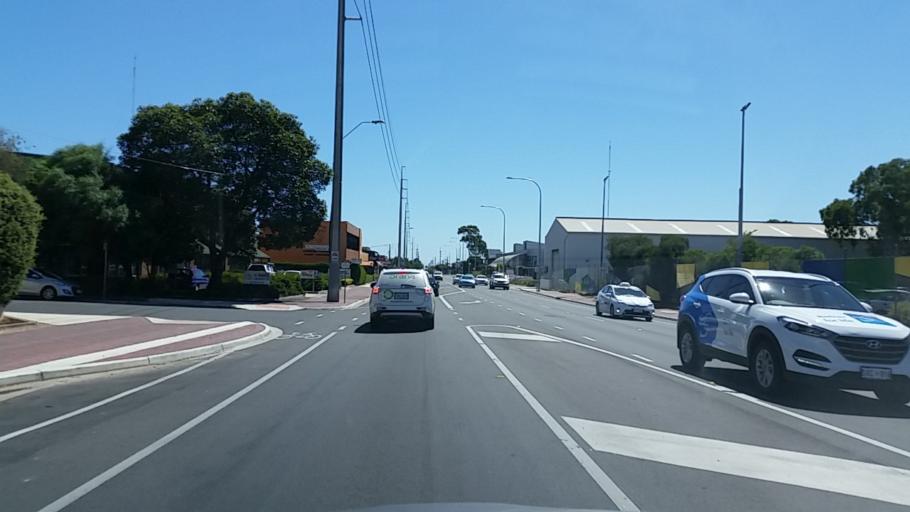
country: AU
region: South Australia
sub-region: Unley
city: Forestville
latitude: -34.9419
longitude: 138.5750
